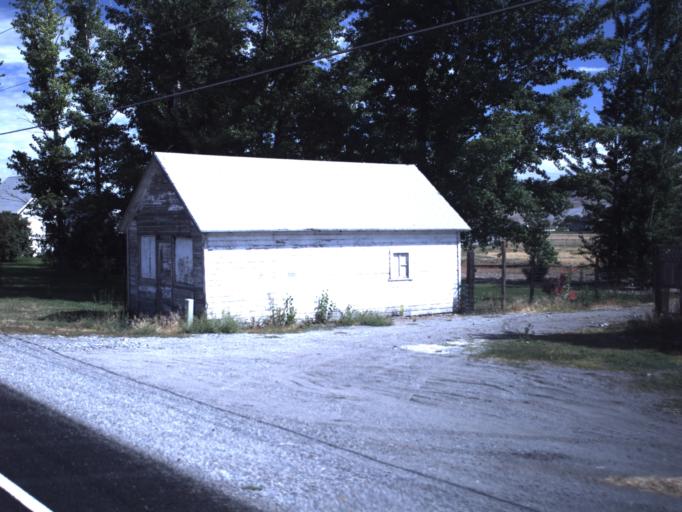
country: US
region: Utah
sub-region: Box Elder County
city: Tremonton
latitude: 41.7167
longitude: -112.1425
